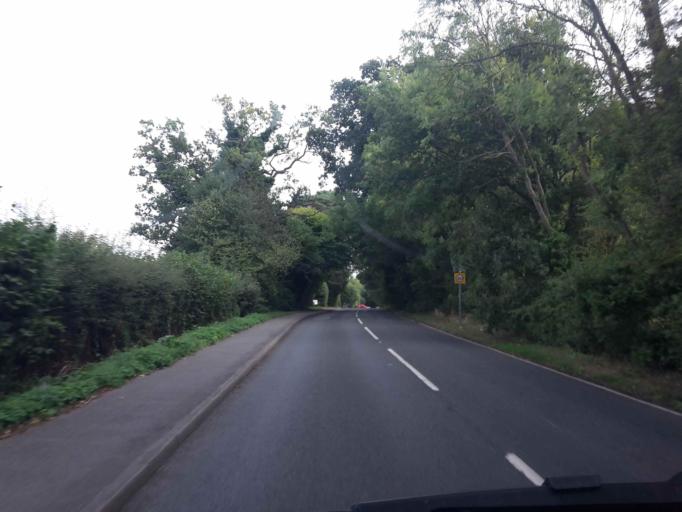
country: GB
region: England
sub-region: Wokingham
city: Wokingham
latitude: 51.4031
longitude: -0.8175
